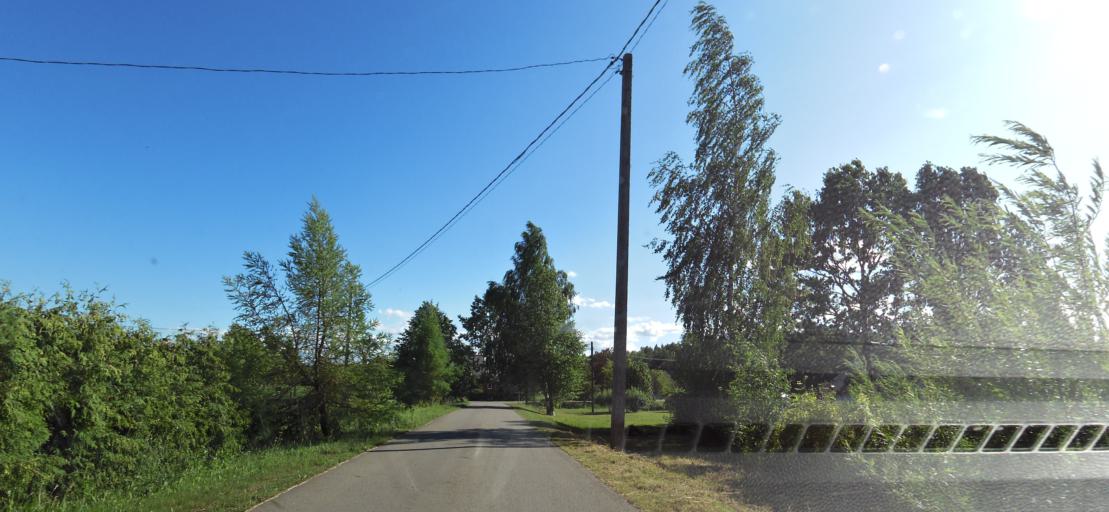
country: LT
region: Panevezys
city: Pasvalys
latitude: 56.1545
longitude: 24.4444
